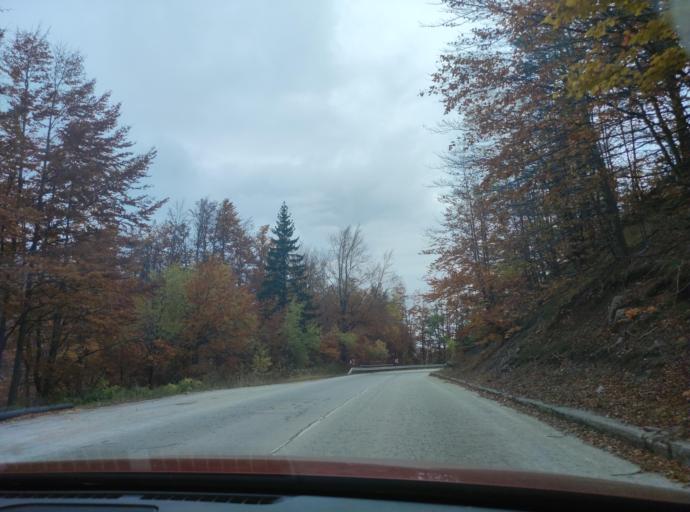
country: BG
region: Montana
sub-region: Obshtina Berkovitsa
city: Berkovitsa
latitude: 43.1306
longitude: 23.1347
